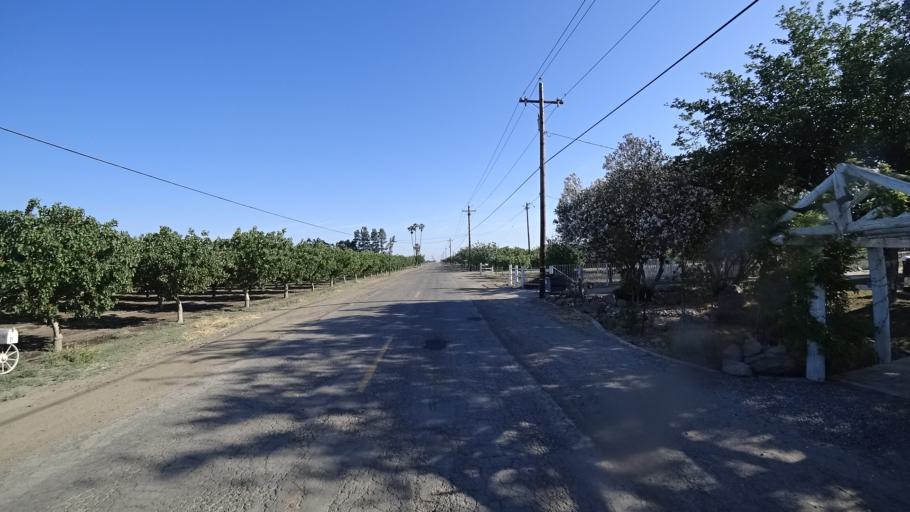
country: US
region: California
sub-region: Kings County
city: Corcoran
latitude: 36.1147
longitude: -119.5543
